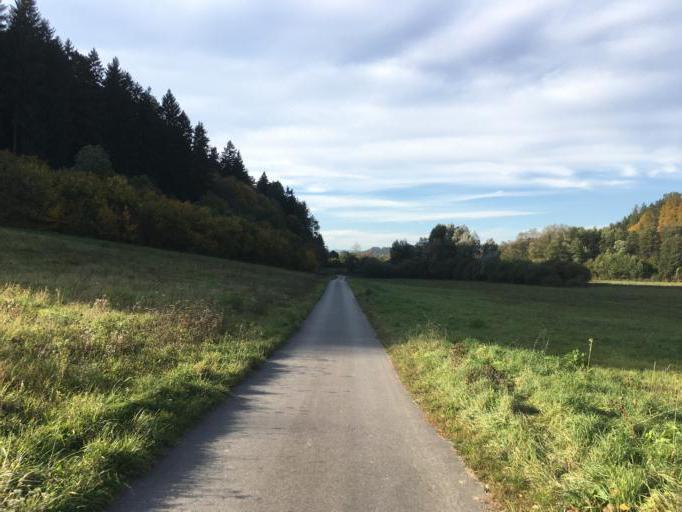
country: SK
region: Trenciansky
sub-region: Okres Povazska Bystrica
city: Povazska Bystrica
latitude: 49.0577
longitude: 18.3939
